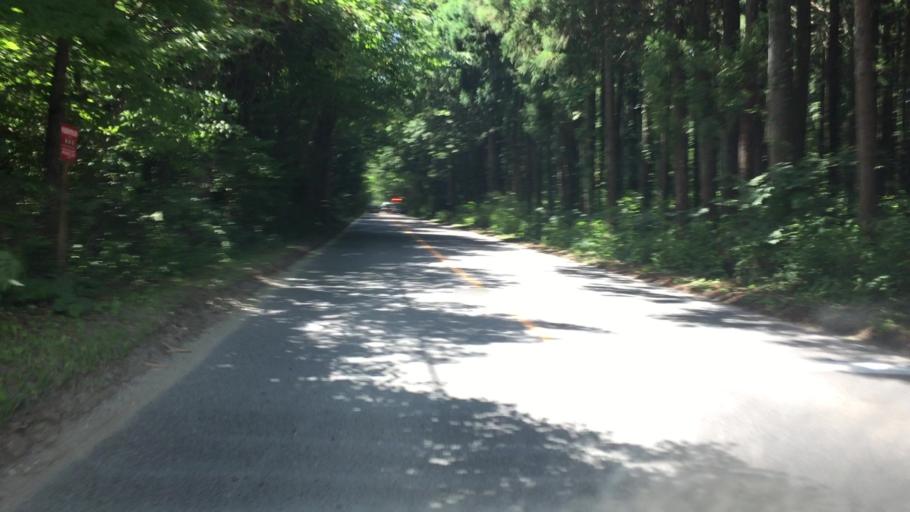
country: JP
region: Tochigi
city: Kuroiso
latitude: 37.0330
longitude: 139.9895
